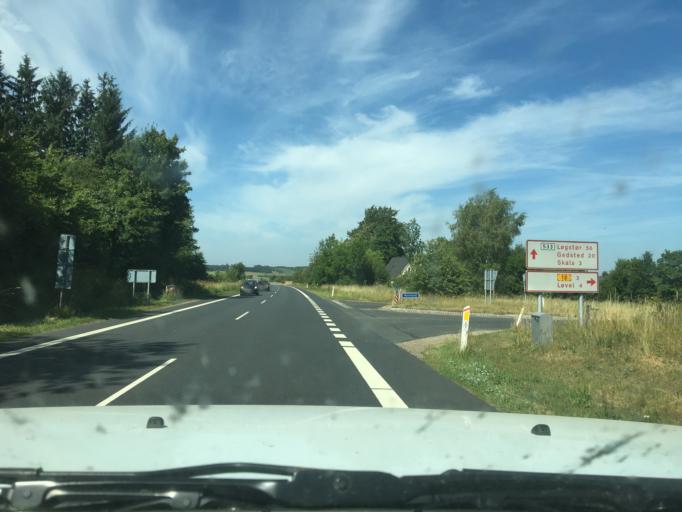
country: DK
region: Central Jutland
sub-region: Viborg Kommune
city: Viborg
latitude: 56.5254
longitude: 9.4046
